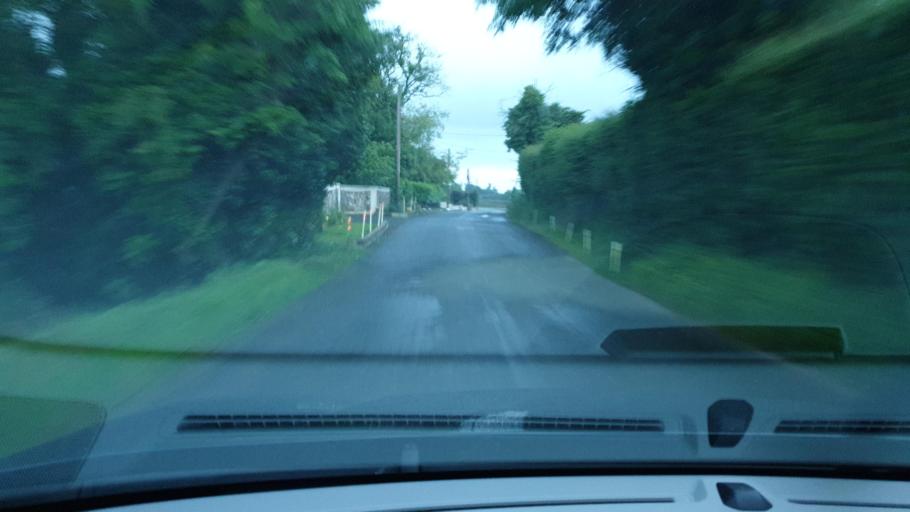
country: IE
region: Leinster
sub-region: An Mhi
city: Ashbourne
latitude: 53.5318
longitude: -6.3387
